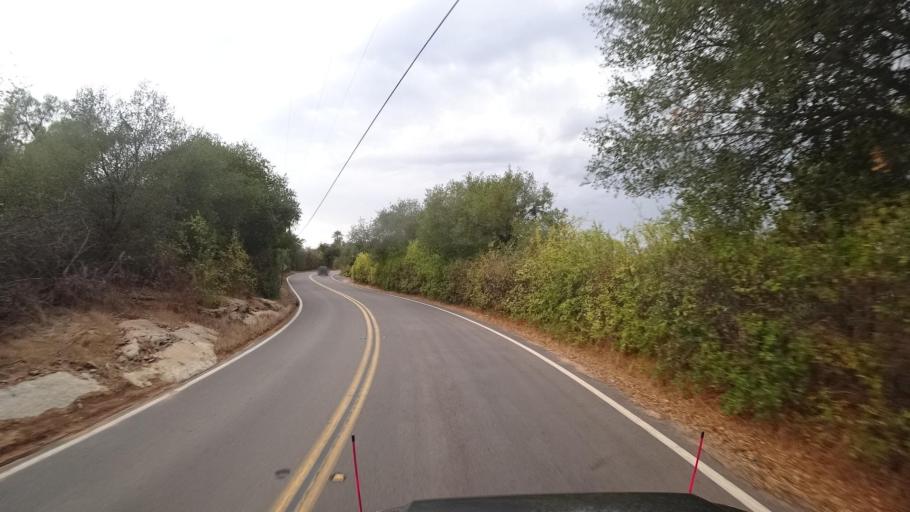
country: US
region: California
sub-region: San Diego County
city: San Pasqual
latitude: 33.0632
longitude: -116.9806
